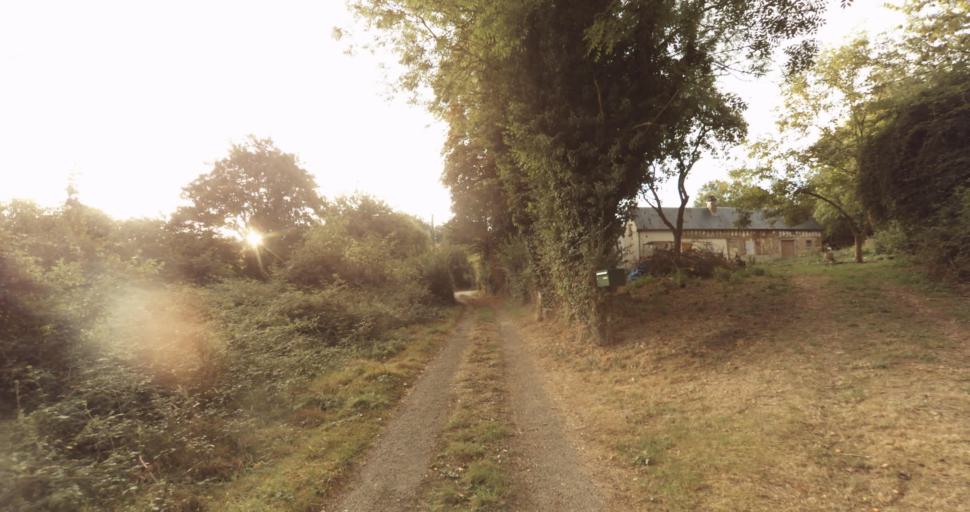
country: FR
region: Lower Normandy
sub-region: Departement de l'Orne
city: Vimoutiers
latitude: 48.9416
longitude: 0.2082
